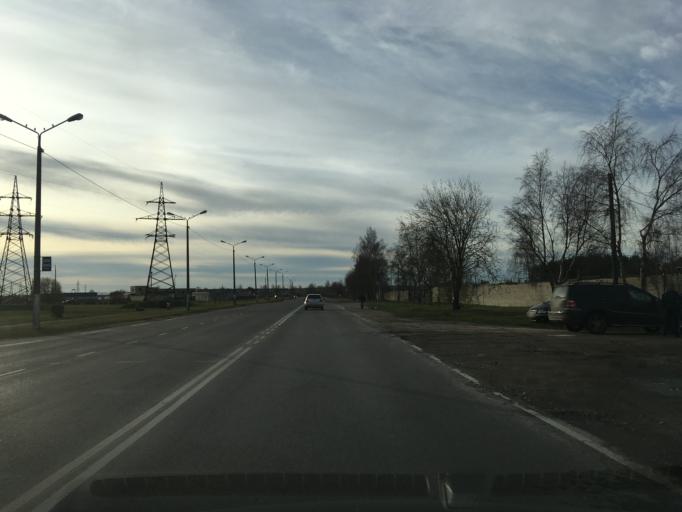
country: EE
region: Ida-Virumaa
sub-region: Narva linn
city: Narva
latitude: 59.3812
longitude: 28.1572
